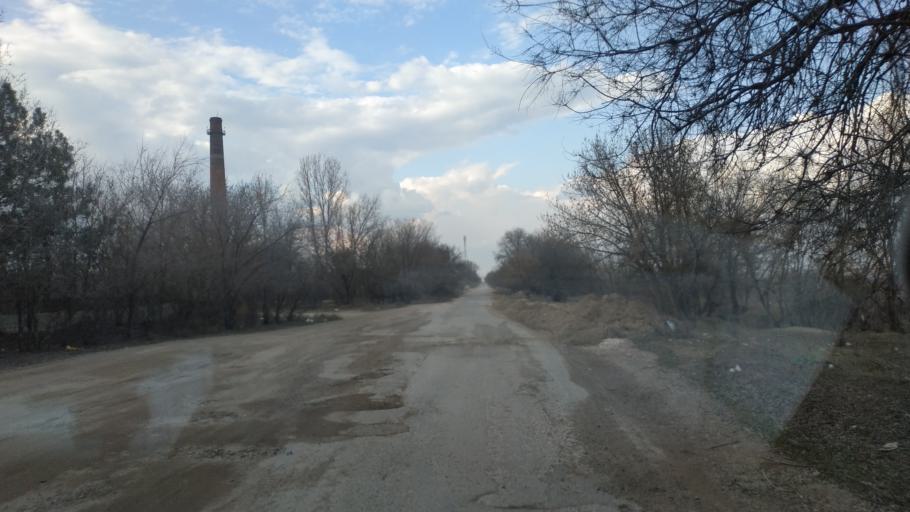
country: MD
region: Anenii Noi
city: Varnita
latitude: 46.8955
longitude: 29.4612
